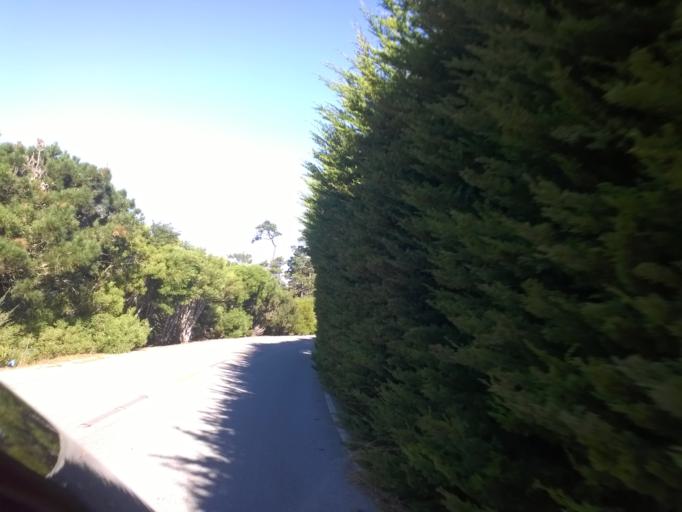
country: US
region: California
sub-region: Monterey County
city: Del Monte Forest
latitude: 36.5774
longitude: -121.9312
